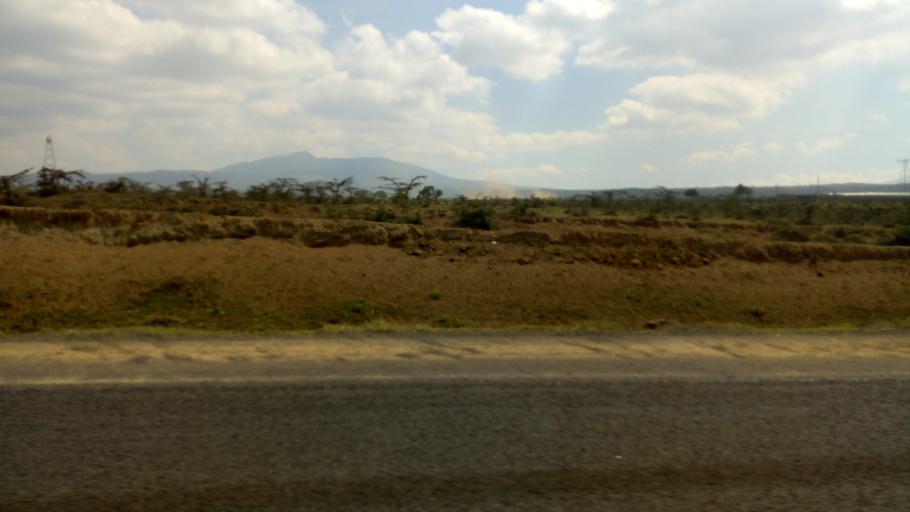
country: KE
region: Nakuru
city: Kijabe
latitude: -1.0129
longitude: 36.4859
